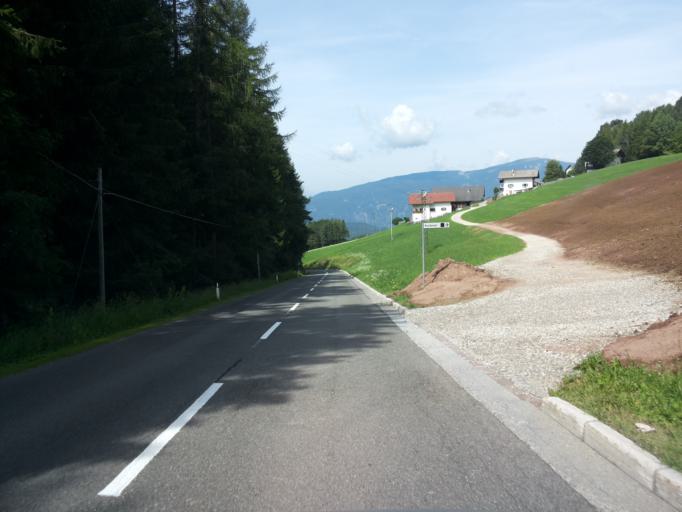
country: IT
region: Trentino-Alto Adige
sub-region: Bolzano
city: Ortisei
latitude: 46.5802
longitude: 11.6203
